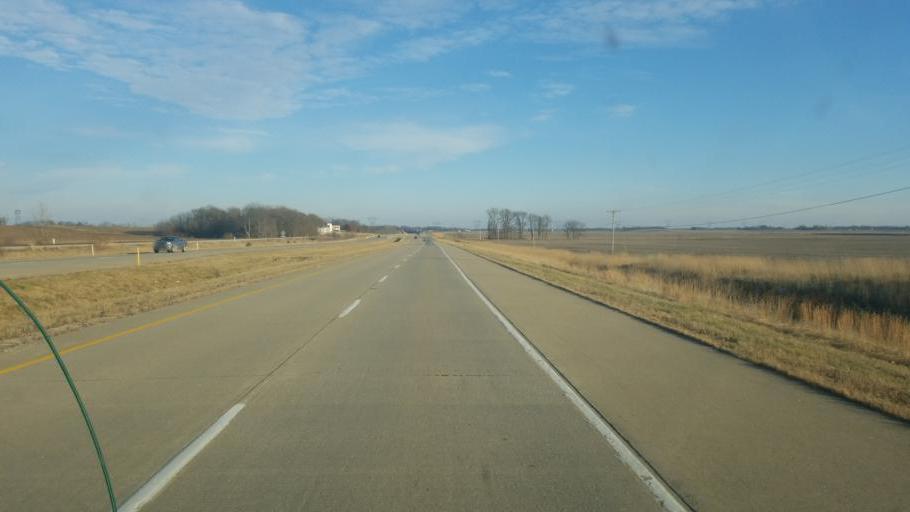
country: US
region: Indiana
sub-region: Knox County
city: Bicknell
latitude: 38.6723
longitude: -87.3549
